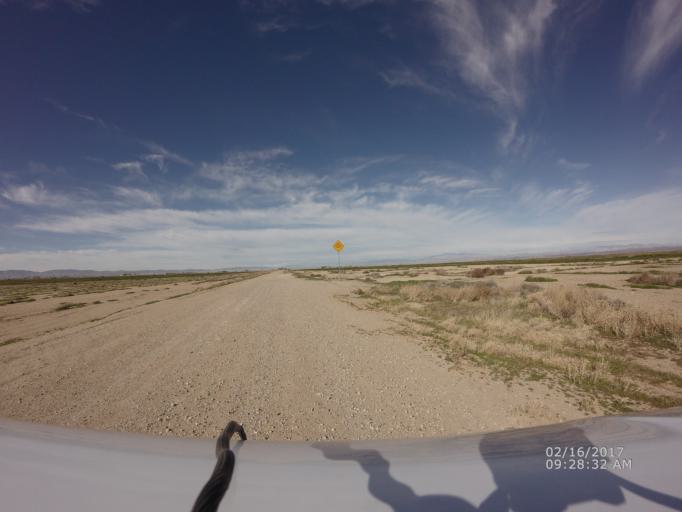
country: US
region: California
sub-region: Kern County
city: Edwards Air Force Base
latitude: 34.7564
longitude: -117.9808
